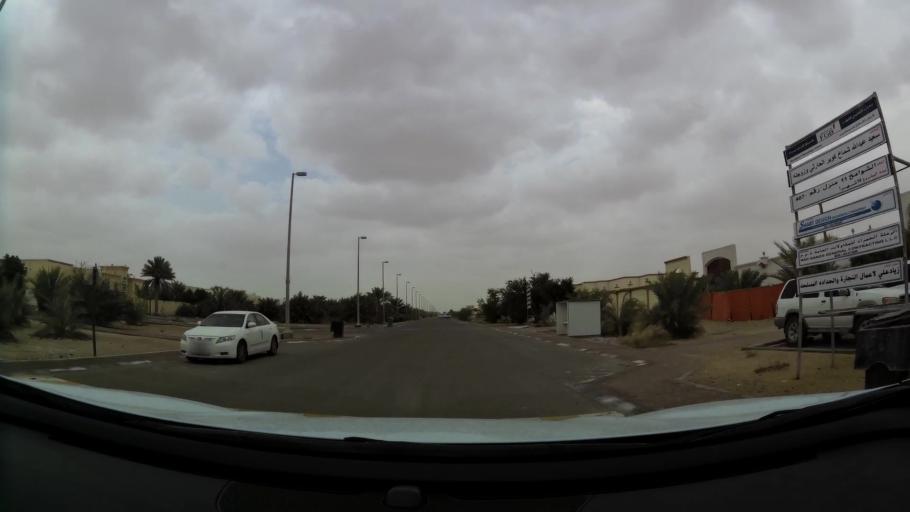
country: AE
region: Abu Dhabi
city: Abu Dhabi
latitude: 24.3280
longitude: 54.6409
